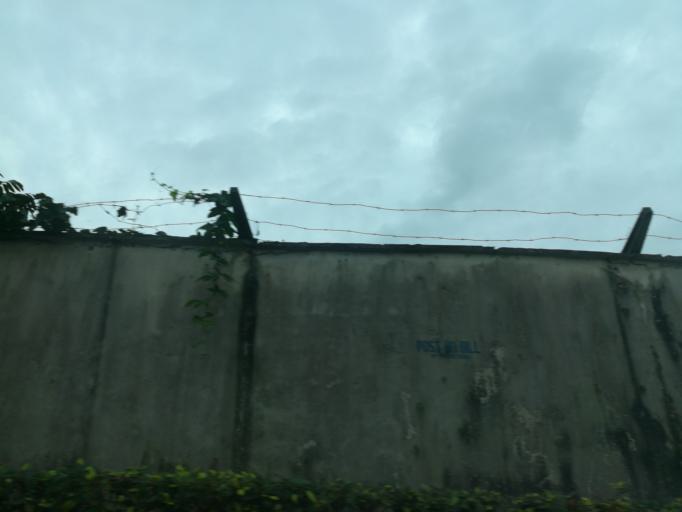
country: NG
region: Rivers
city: Port Harcourt
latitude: 4.8348
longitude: 7.0205
